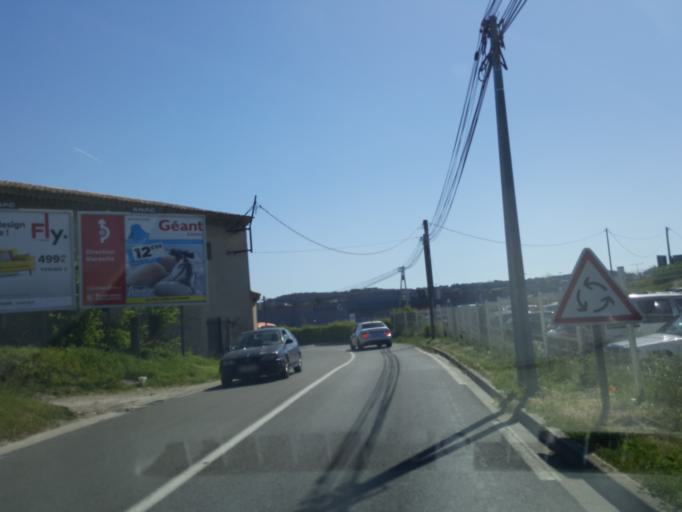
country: FR
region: Provence-Alpes-Cote d'Azur
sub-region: Departement des Bouches-du-Rhone
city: Cabries
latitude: 43.4231
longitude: 5.3678
